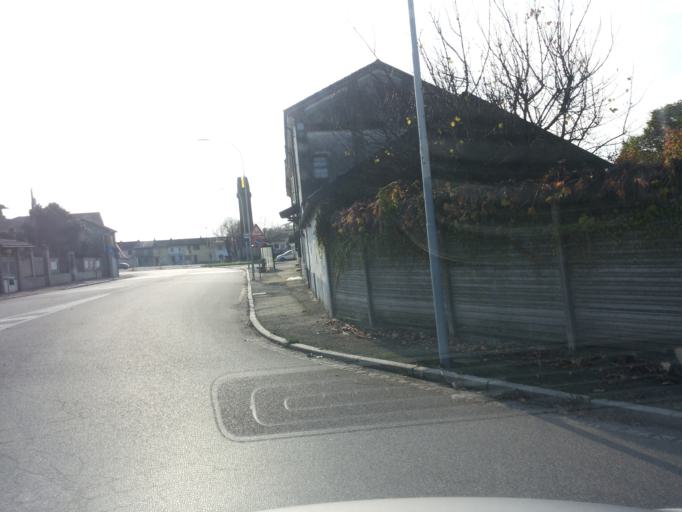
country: IT
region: Piedmont
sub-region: Provincia di Vercelli
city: Caresana
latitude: 45.2224
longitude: 8.5027
